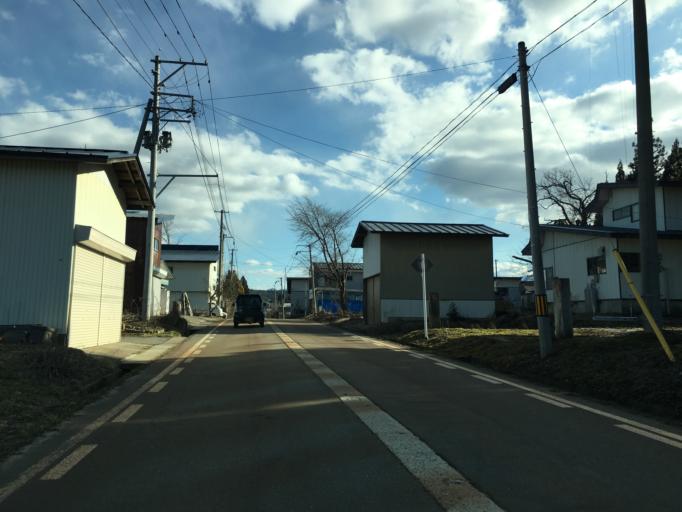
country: JP
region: Yamagata
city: Yonezawa
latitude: 37.9619
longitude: 139.9891
